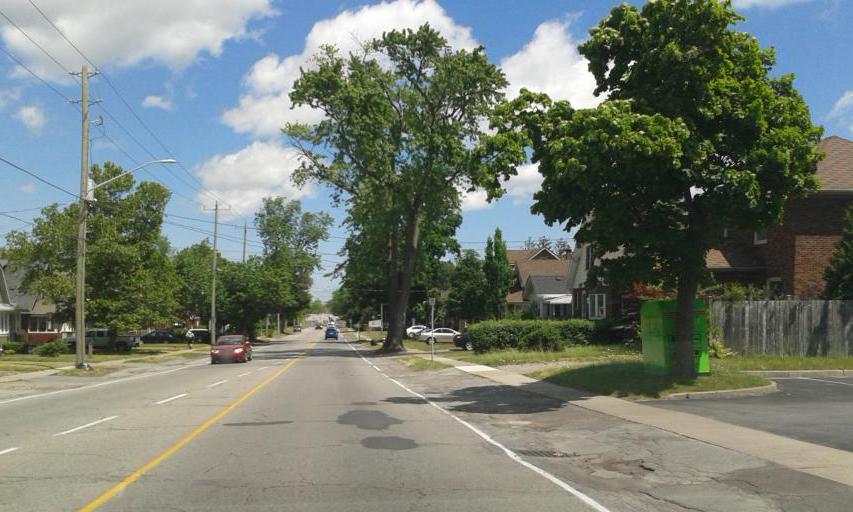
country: CA
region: Ontario
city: Niagara Falls
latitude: 43.0896
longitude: -79.1106
